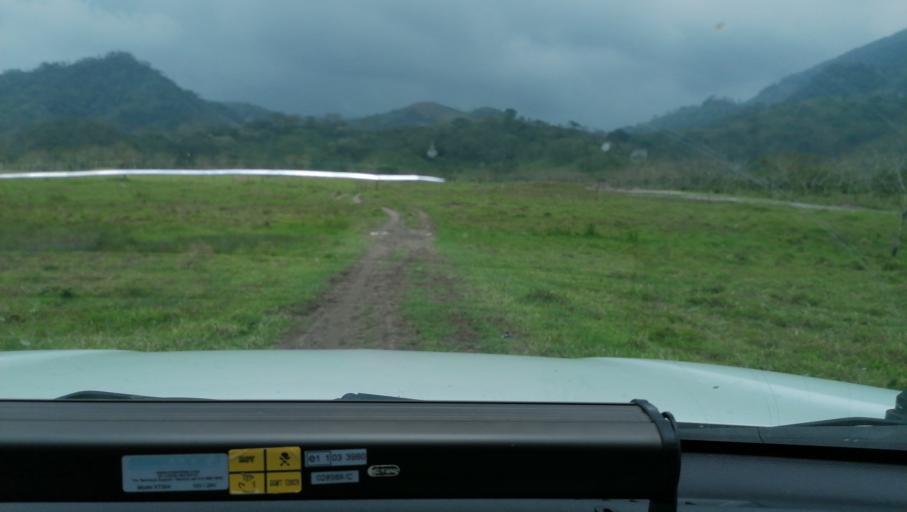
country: MX
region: Chiapas
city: Ixtacomitan
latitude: 17.3635
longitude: -93.1851
